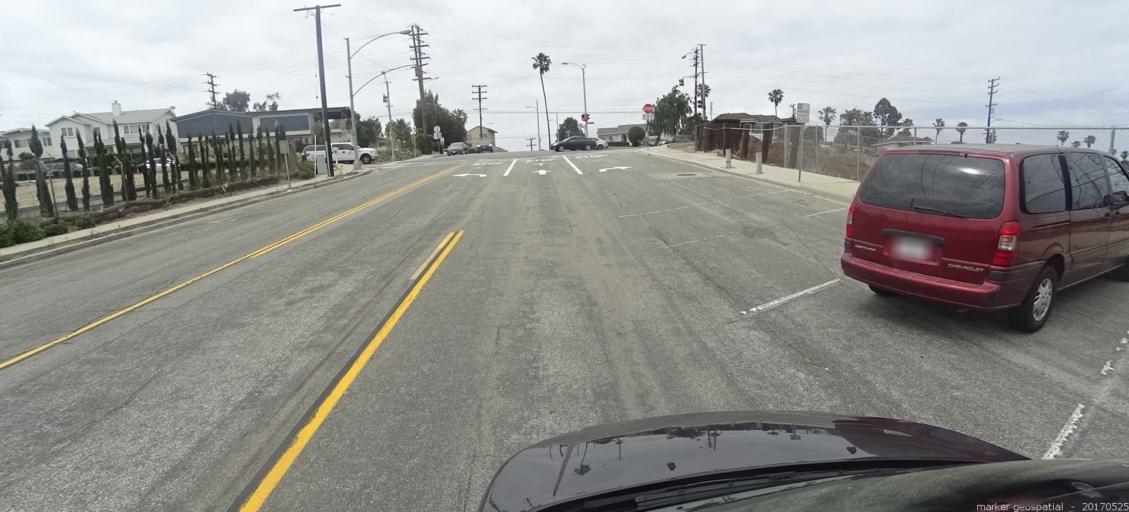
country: US
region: California
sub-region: Los Angeles County
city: Redondo Beach
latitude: 33.8576
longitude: -118.3787
